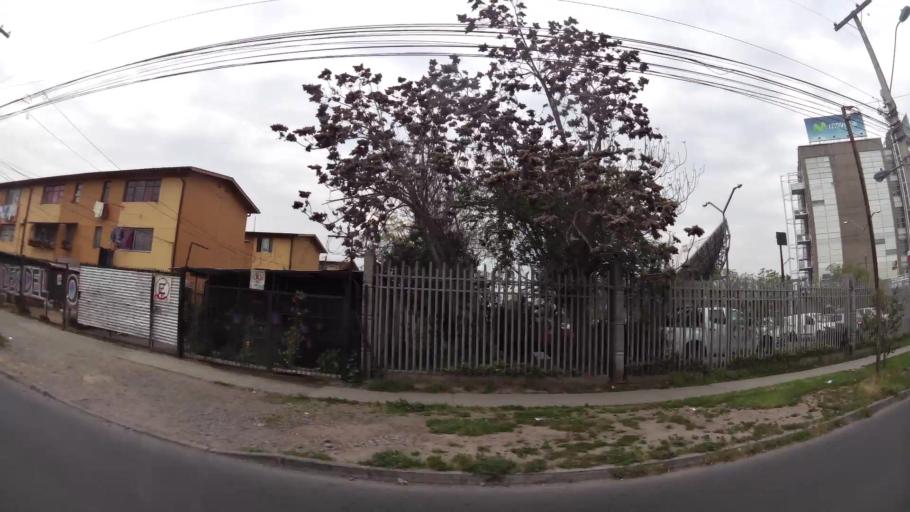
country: CL
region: Santiago Metropolitan
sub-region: Provincia de Santiago
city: Villa Presidente Frei, Nunoa, Santiago, Chile
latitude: -33.5048
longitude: -70.6035
